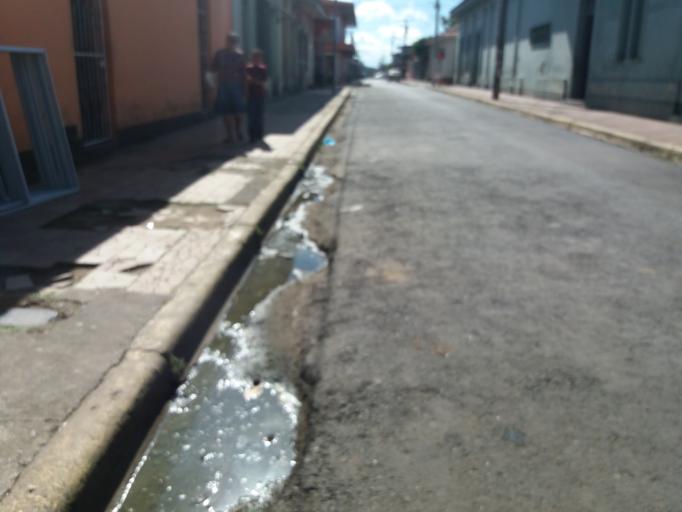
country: NI
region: Carazo
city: Jinotepe
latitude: 11.8475
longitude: -86.1965
